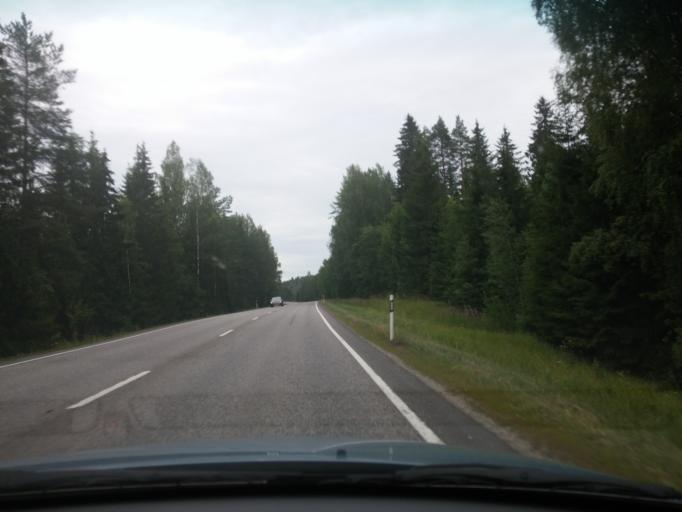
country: FI
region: Haeme
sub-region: Riihimaeki
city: Loppi
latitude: 60.7293
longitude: 24.4003
